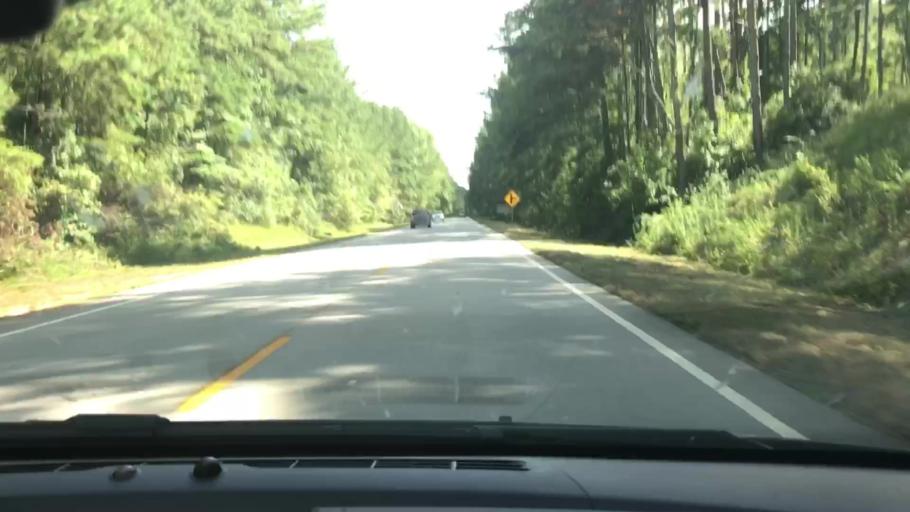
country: US
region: Georgia
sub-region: Troup County
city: La Grange
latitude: 33.1296
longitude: -85.0895
